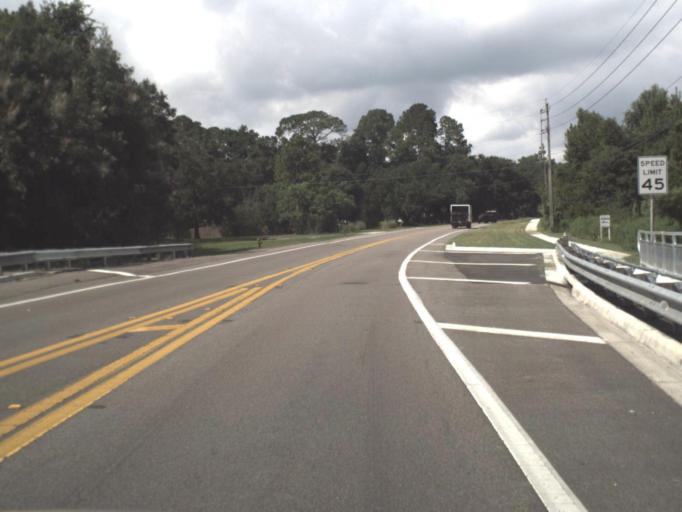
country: US
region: Florida
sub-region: Saint Johns County
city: Fruit Cove
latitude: 30.0905
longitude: -81.6292
